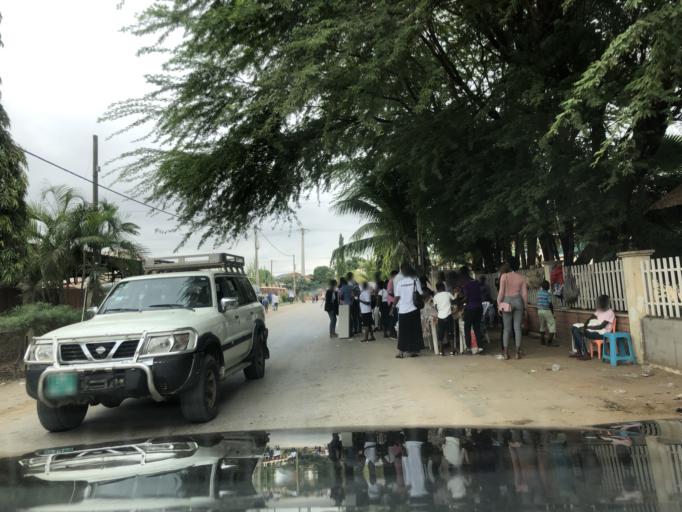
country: AO
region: Luanda
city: Luanda
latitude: -8.9070
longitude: 13.2295
